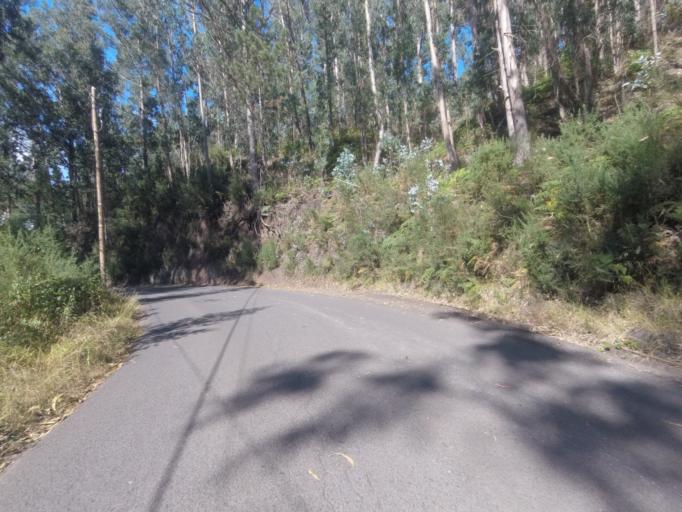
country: PT
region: Madeira
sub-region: Ribeira Brava
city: Campanario
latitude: 32.6893
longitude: -17.0206
